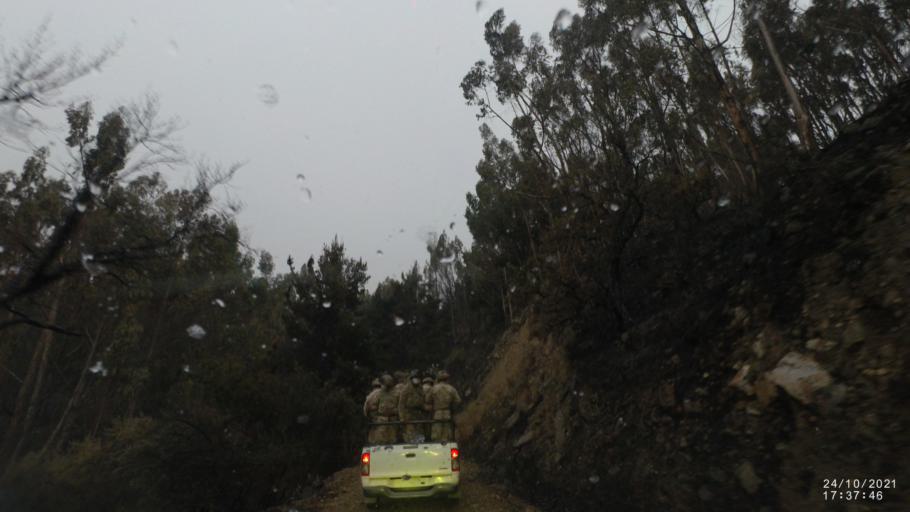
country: BO
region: Cochabamba
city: Cochabamba
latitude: -17.3183
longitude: -66.1299
